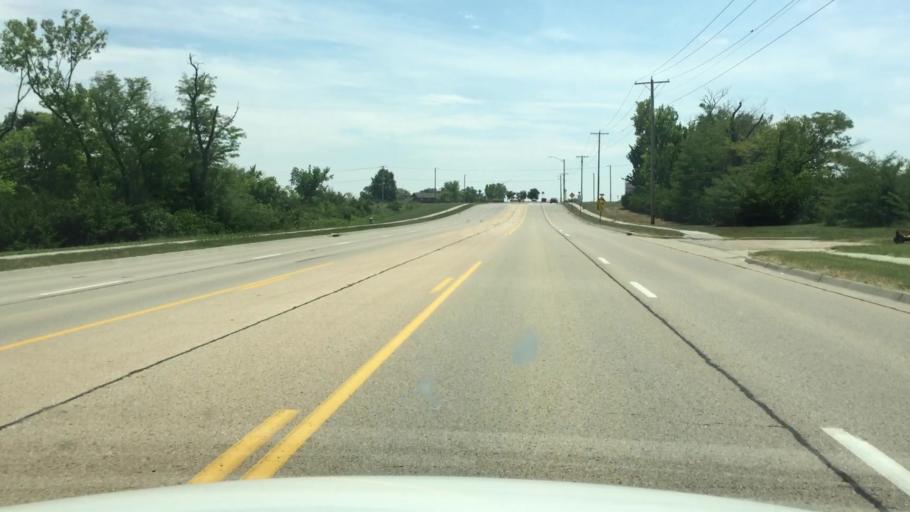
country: US
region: Kansas
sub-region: Shawnee County
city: Topeka
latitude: 38.9886
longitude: -95.6144
